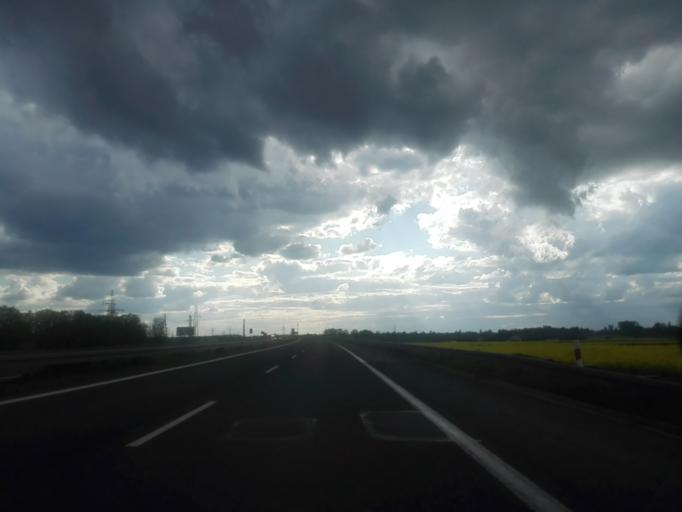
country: PL
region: Masovian Voivodeship
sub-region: Powiat ostrowski
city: Ostrow Mazowiecka
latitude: 52.8207
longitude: 21.9078
